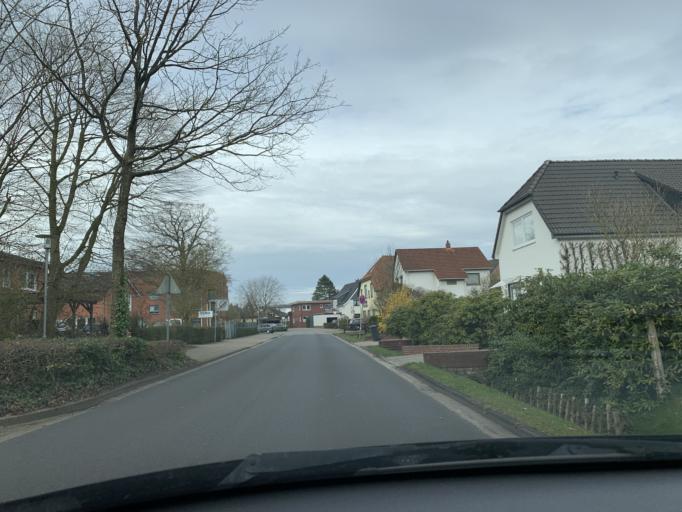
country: DE
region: Lower Saxony
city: Oldenburg
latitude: 53.1278
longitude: 8.1793
